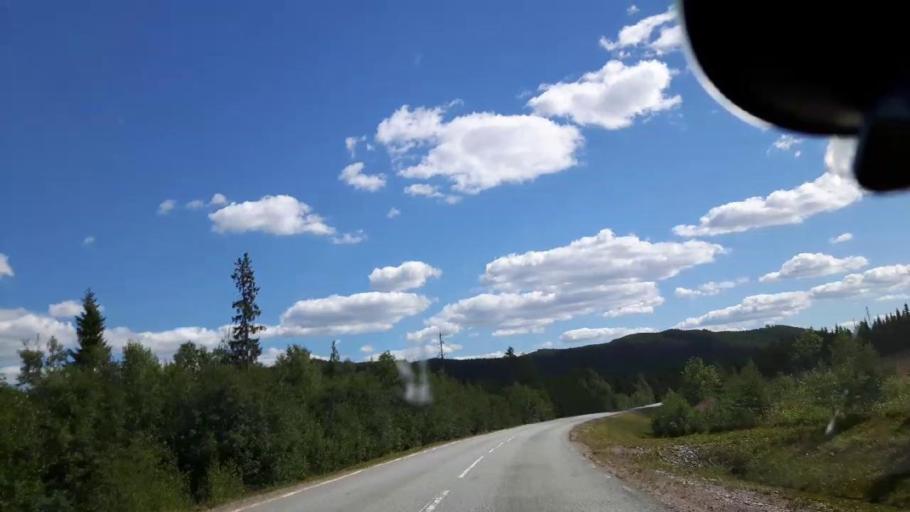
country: SE
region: Jaemtland
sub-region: Ragunda Kommun
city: Hammarstrand
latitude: 62.9573
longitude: 16.2044
